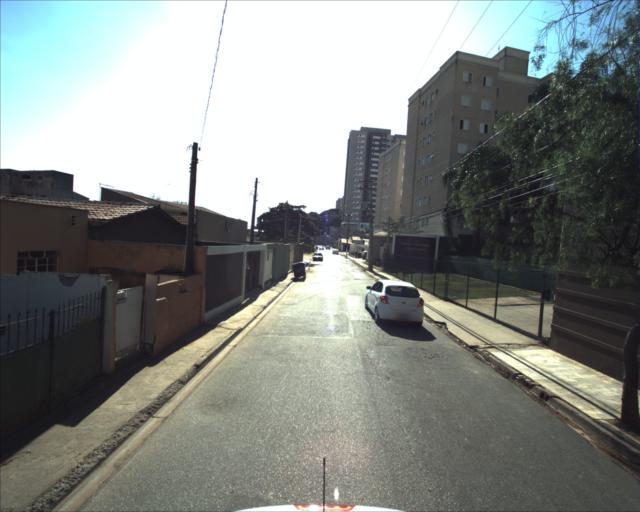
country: BR
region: Sao Paulo
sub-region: Sorocaba
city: Sorocaba
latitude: -23.4942
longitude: -47.4304
